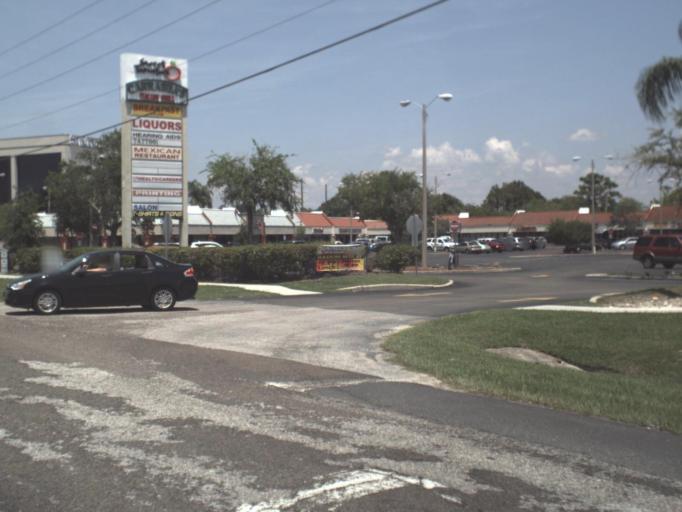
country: US
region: Florida
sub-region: Pasco County
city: Jasmine Estates
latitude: 28.3046
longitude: -82.7026
